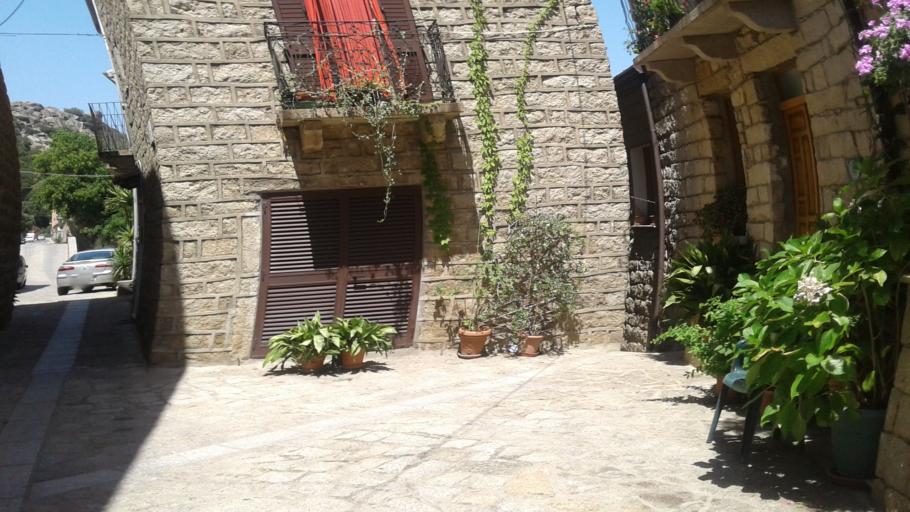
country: IT
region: Sardinia
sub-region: Provincia di Olbia-Tempio
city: Aggius
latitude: 40.9294
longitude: 9.0651
